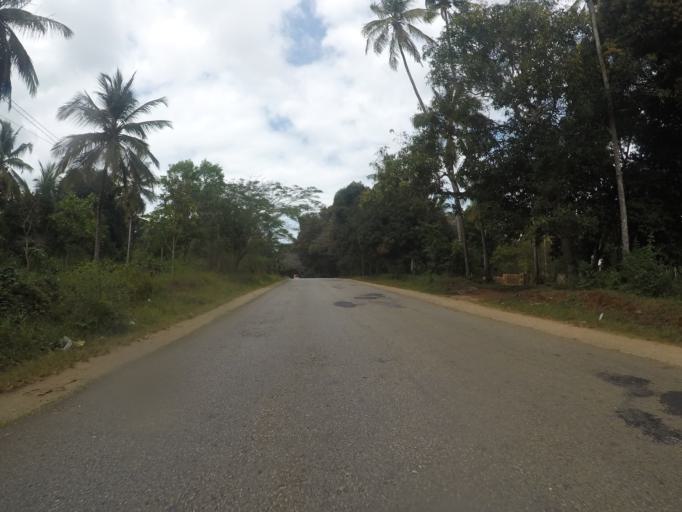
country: TZ
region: Zanzibar Central/South
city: Koani
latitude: -6.2071
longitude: 39.3248
